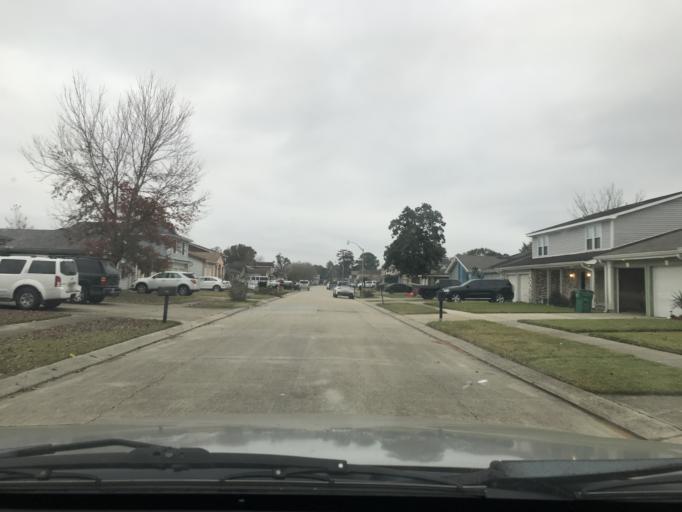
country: US
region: Louisiana
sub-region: Jefferson Parish
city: Woodmere
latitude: 29.8668
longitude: -90.0785
